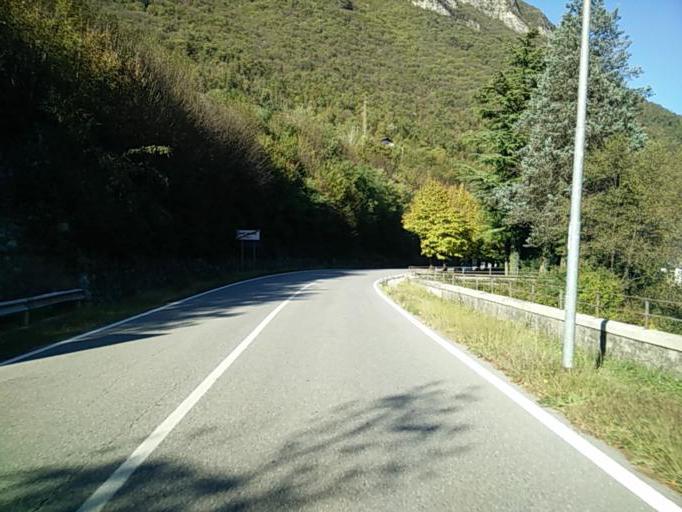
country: IT
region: Lombardy
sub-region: Provincia di Brescia
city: Idro
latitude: 45.7369
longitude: 10.4619
